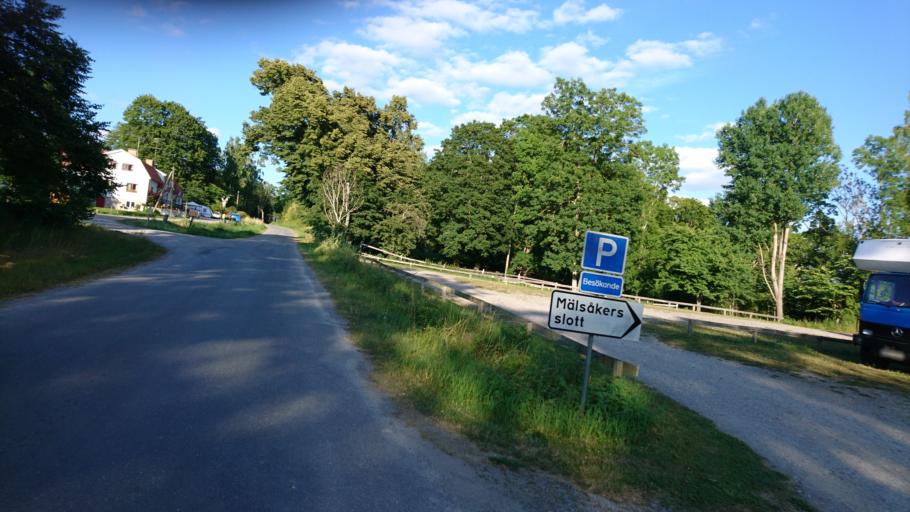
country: SE
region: Soedermanland
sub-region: Strangnas Kommun
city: Stallarholmen
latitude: 59.3850
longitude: 17.3029
